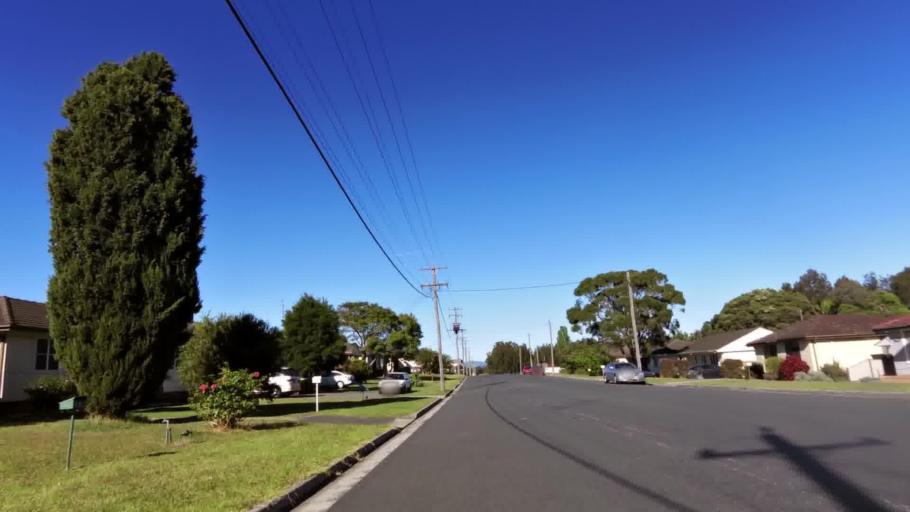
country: AU
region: New South Wales
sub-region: Wollongong
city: Berkeley
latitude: -34.4758
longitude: 150.8344
